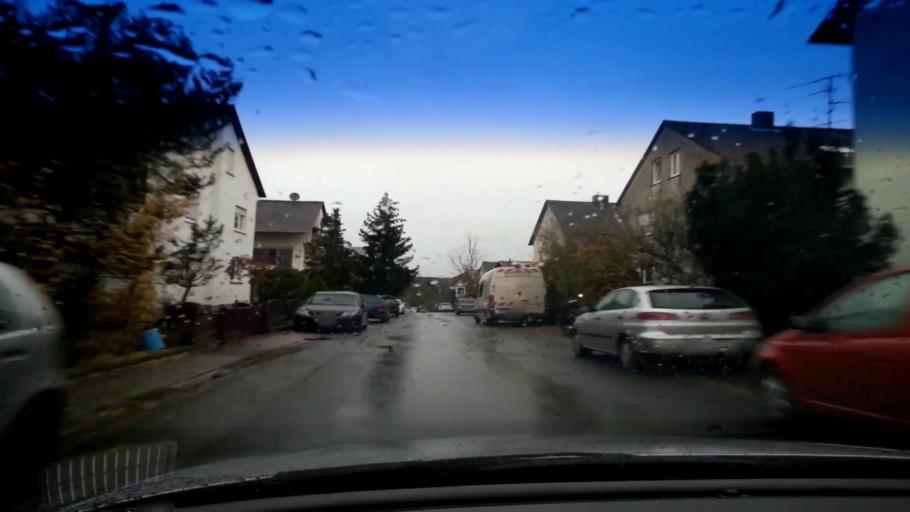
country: DE
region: Bavaria
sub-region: Upper Franconia
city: Hallstadt
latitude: 49.9270
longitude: 10.8845
